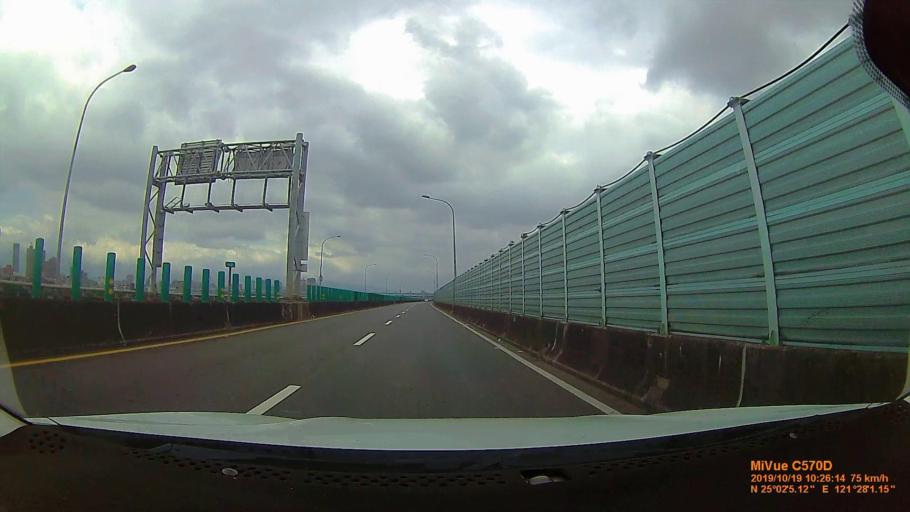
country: TW
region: Taipei
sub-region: Taipei
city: Banqiao
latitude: 25.0358
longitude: 121.4671
